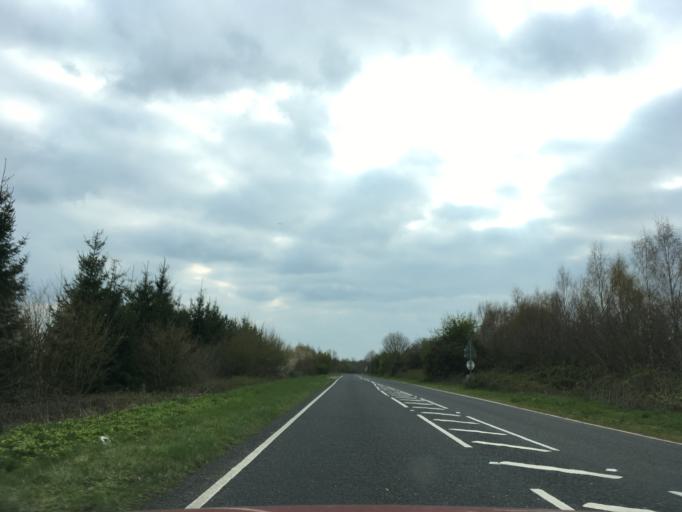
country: GB
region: England
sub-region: Oxfordshire
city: Burford
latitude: 51.8033
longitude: -1.6732
